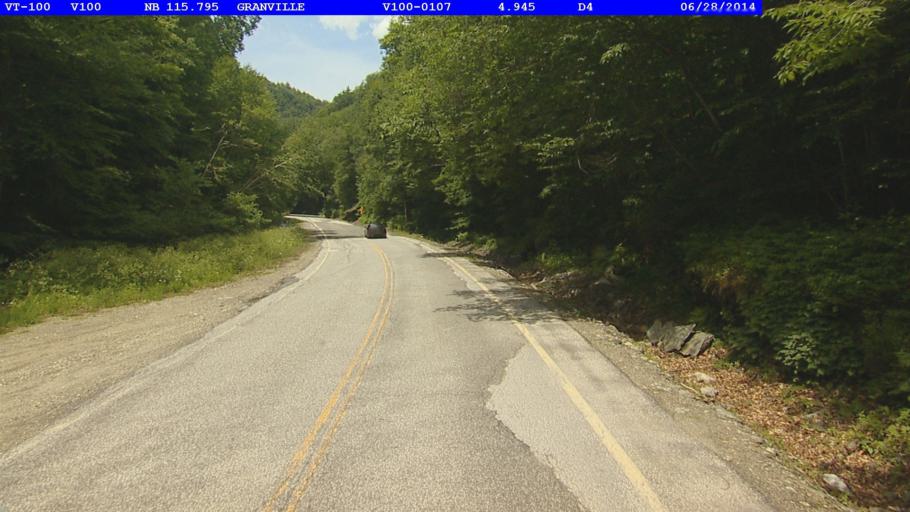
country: US
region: Vermont
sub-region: Orange County
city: Randolph
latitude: 44.0101
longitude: -72.8480
